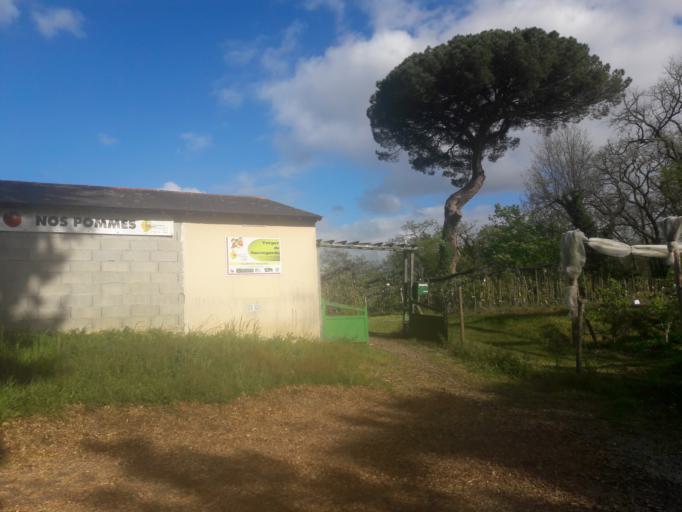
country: FR
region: Pays de la Loire
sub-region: Departement de la Loire-Atlantique
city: Nort-sur-Erdre
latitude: 47.4381
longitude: -1.5044
